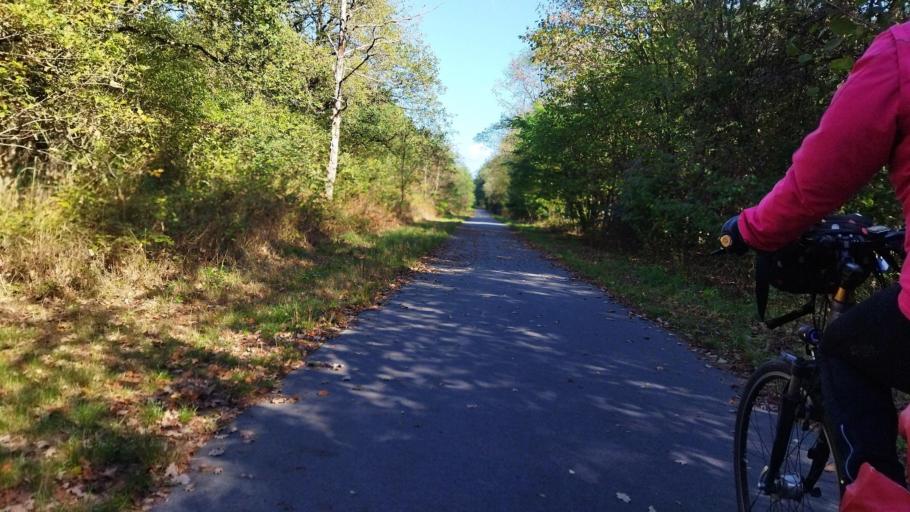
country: DE
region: Lower Saxony
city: Ohne
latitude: 52.2674
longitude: 7.3141
